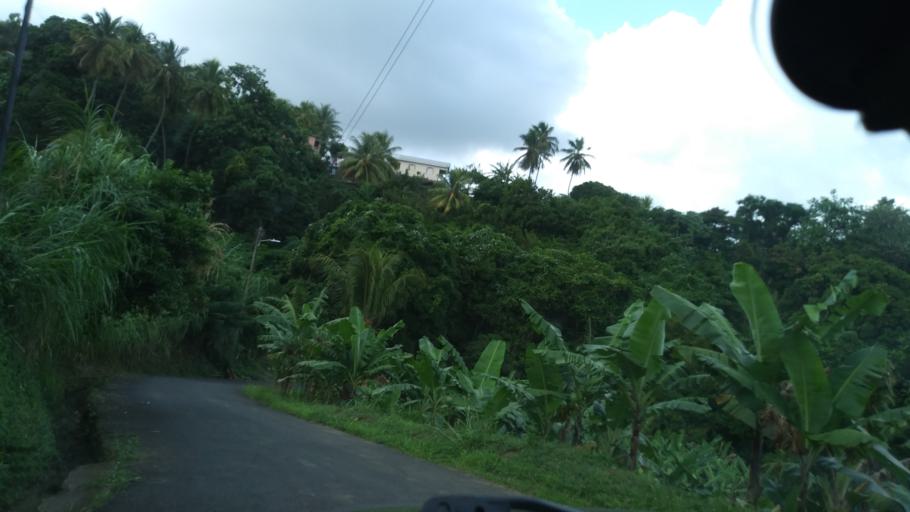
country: VC
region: Charlotte
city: Byera Village
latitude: 13.2314
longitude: -61.1356
